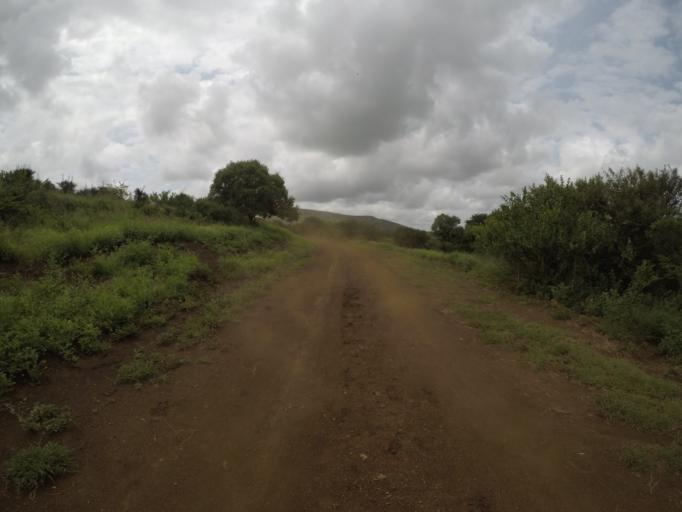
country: ZA
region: KwaZulu-Natal
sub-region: uThungulu District Municipality
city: Empangeni
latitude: -28.5950
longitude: 31.8777
